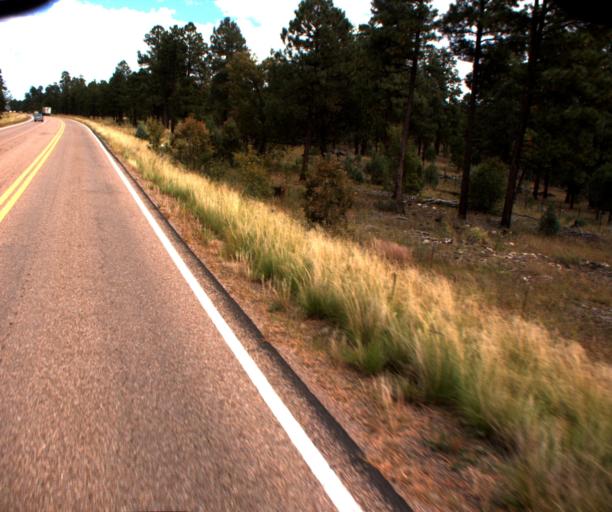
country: US
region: Arizona
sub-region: Navajo County
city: Heber-Overgaard
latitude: 34.3745
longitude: -110.6787
